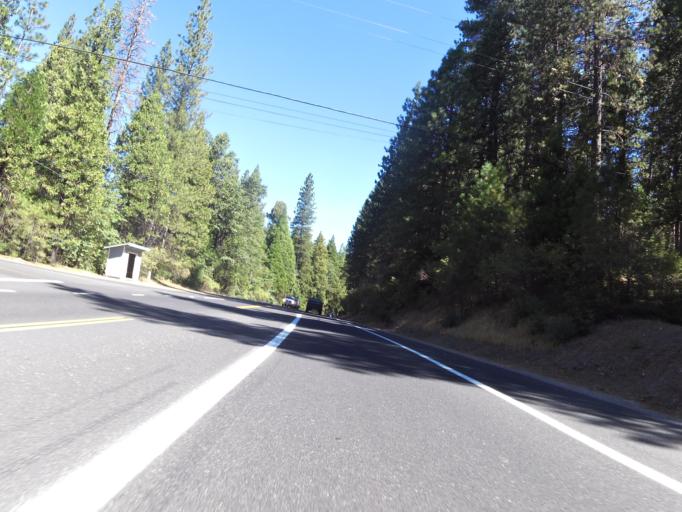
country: US
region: California
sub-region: Calaveras County
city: Arnold
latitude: 38.2356
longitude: -120.3650
